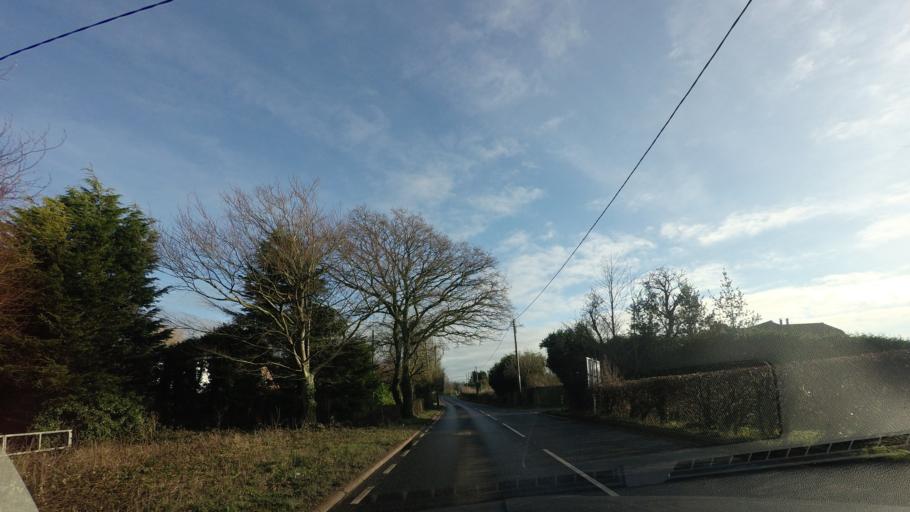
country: GB
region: England
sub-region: East Sussex
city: Bexhill-on-Sea
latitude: 50.8742
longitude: 0.4327
